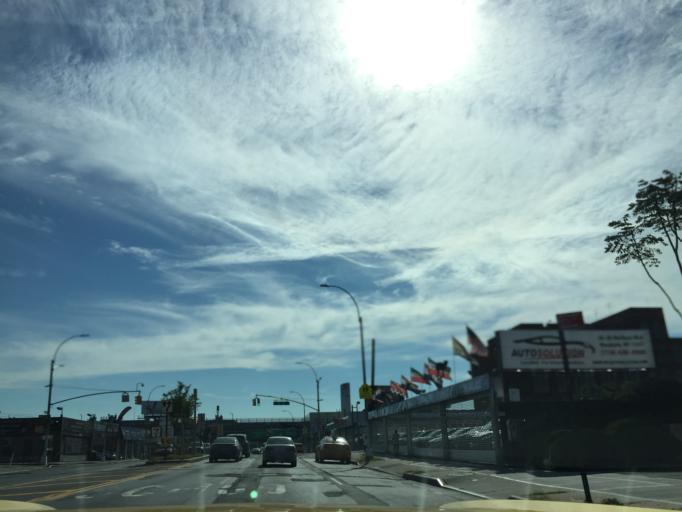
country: US
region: New York
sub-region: Queens County
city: Long Island City
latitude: 40.7538
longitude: -73.9019
